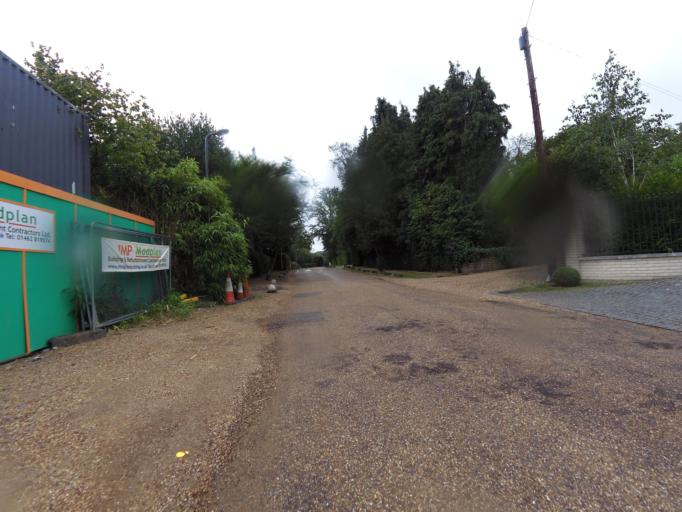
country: GB
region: England
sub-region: Hertfordshire
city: Radlett
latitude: 51.6881
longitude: -0.3246
